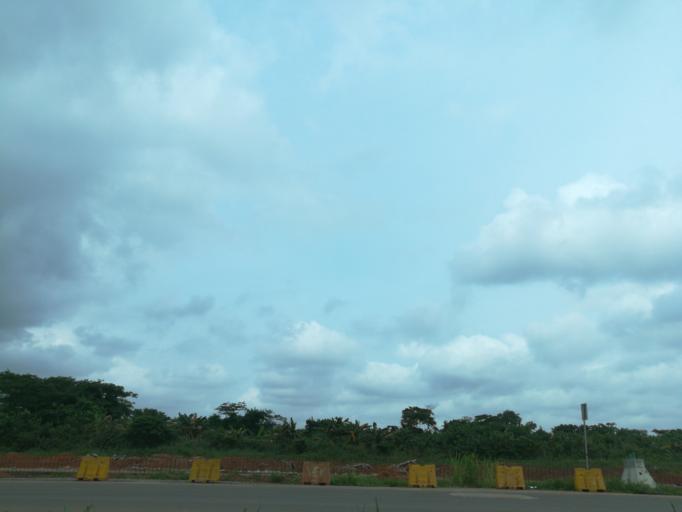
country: NG
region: Lagos
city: Oshodi
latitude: 6.5720
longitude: 3.3215
